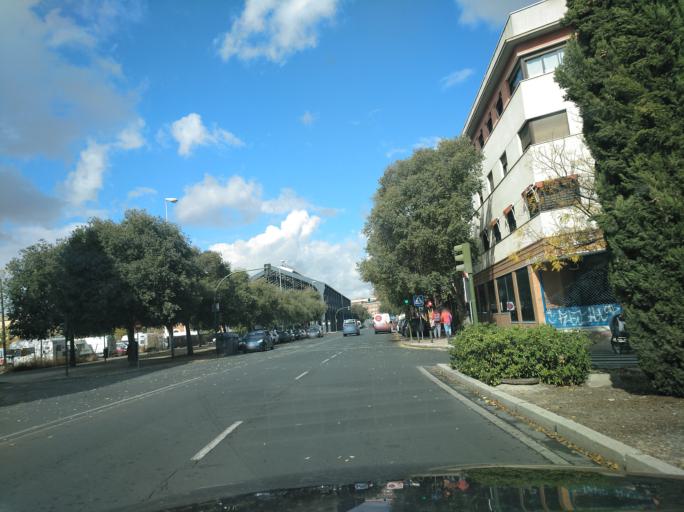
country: ES
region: Andalusia
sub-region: Provincia de Sevilla
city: Sevilla
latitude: 37.3814
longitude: -5.9835
